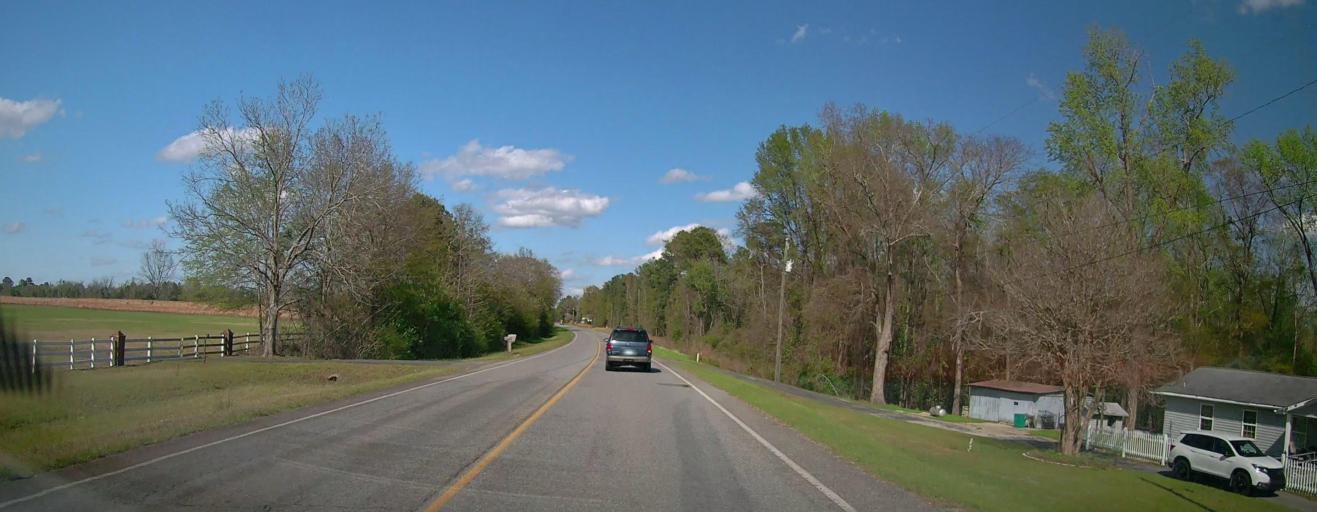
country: US
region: Georgia
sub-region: Baldwin County
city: Hardwick
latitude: 33.0112
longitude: -83.2427
